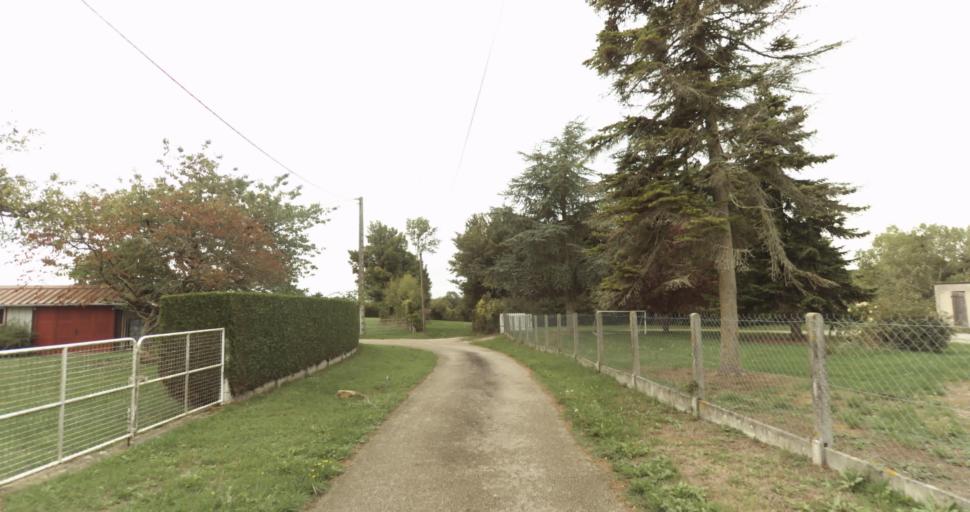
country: FR
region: Lower Normandy
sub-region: Departement de l'Orne
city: Gace
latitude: 48.6846
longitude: 0.3075
